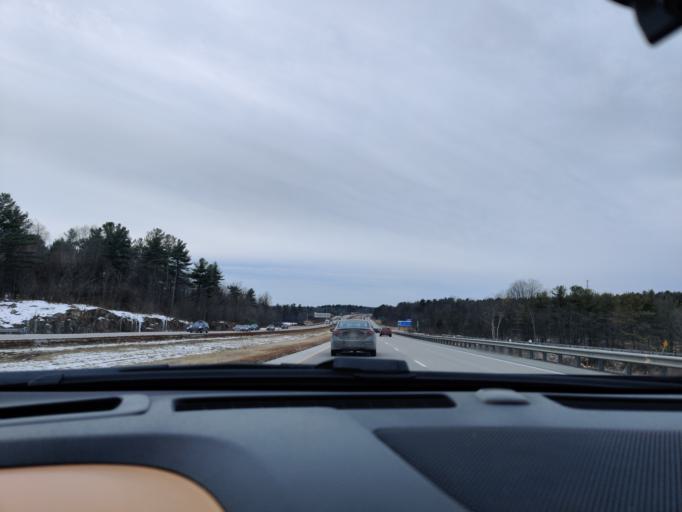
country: US
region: New York
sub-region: Jefferson County
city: Alexandria Bay
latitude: 44.3809
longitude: -75.9891
